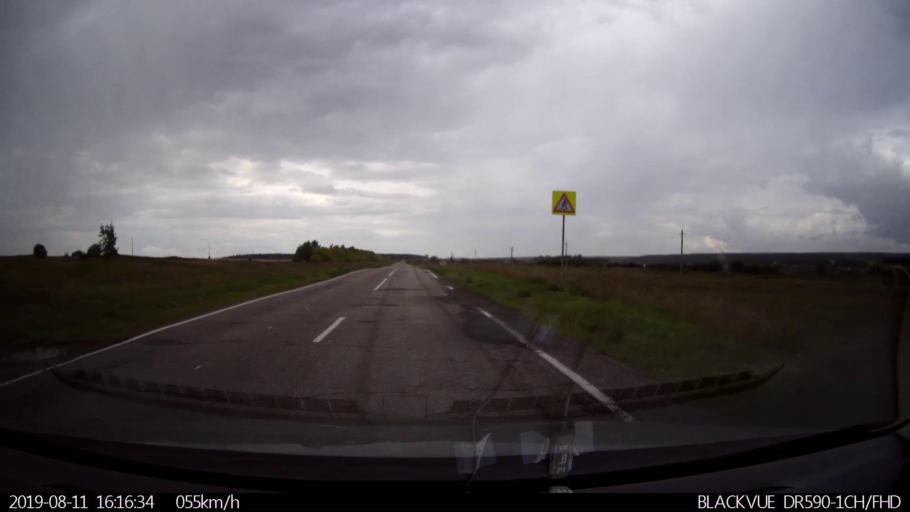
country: RU
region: Ulyanovsk
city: Mayna
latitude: 54.0420
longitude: 47.6207
